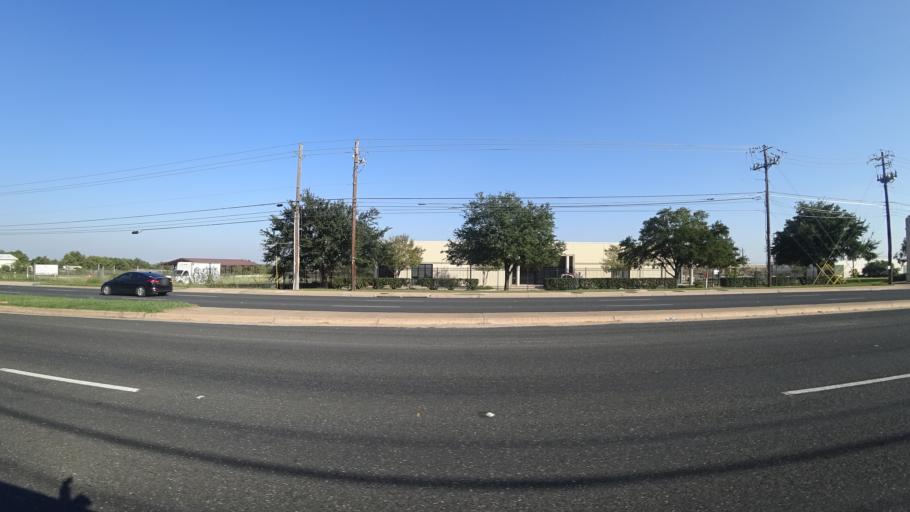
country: US
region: Texas
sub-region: Travis County
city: Wells Branch
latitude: 30.3554
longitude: -97.6732
